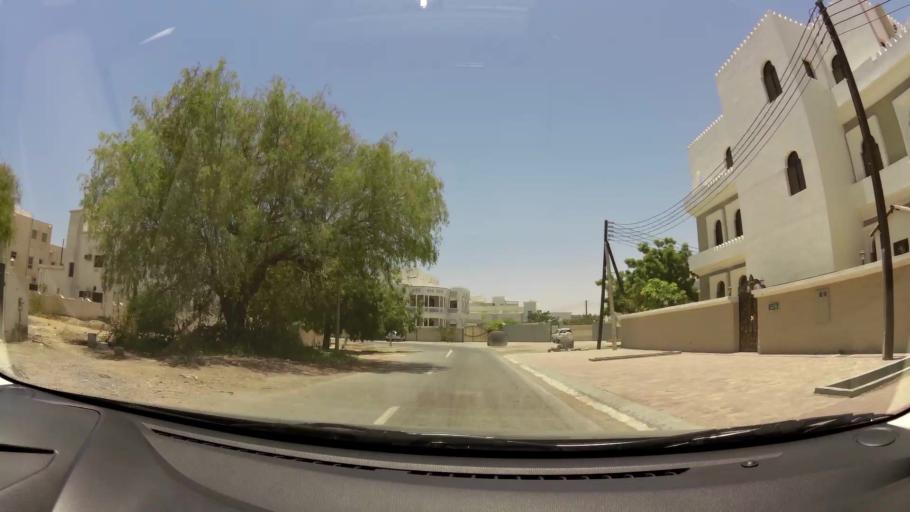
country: OM
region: Muhafazat Masqat
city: As Sib al Jadidah
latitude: 23.6377
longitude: 58.2346
